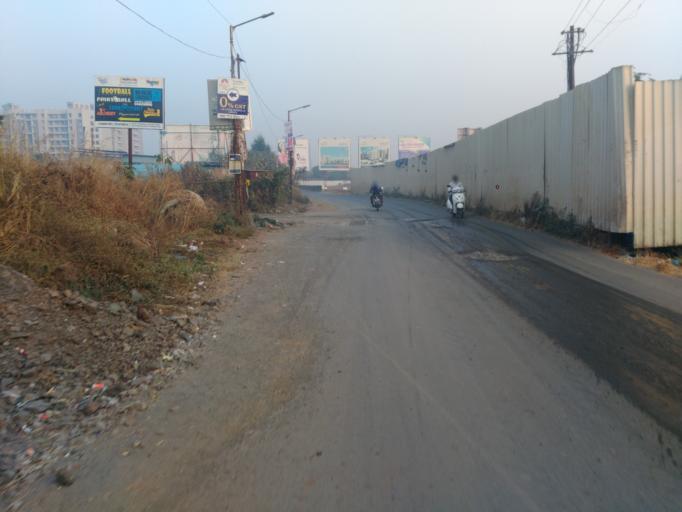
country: IN
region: Maharashtra
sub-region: Pune Division
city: Pune
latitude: 18.4472
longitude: 73.8856
